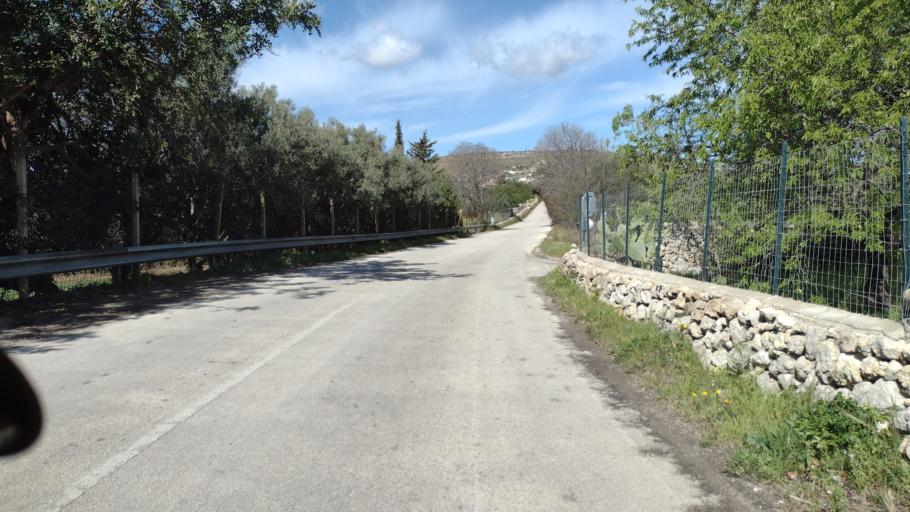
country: IT
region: Sicily
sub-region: Provincia di Siracusa
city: Noto
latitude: 36.9021
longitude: 15.0398
